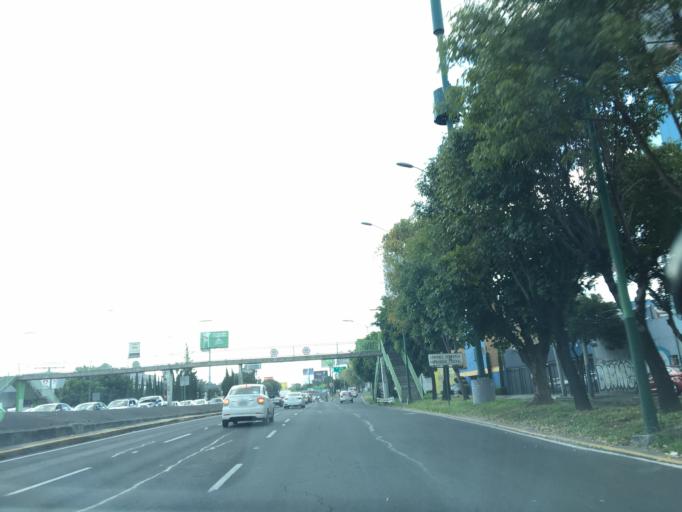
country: MX
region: Mexico City
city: Mexico City
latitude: 19.4050
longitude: -99.1234
